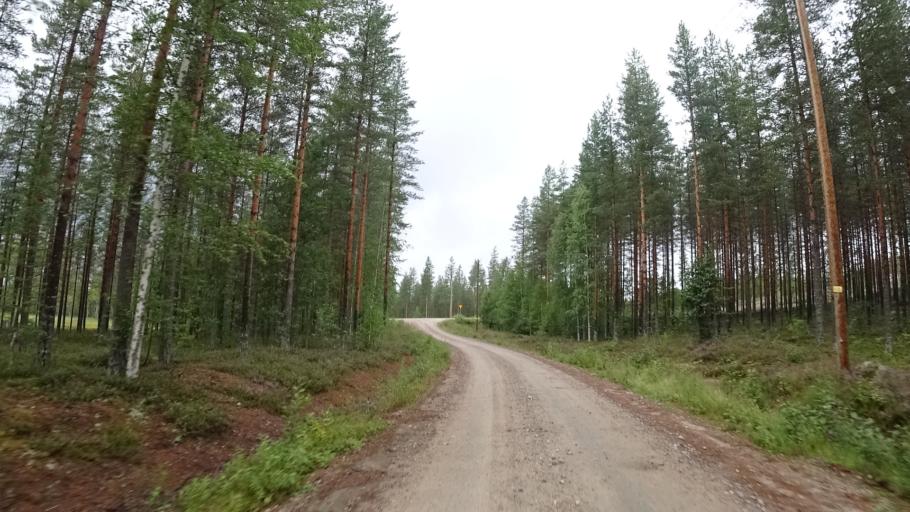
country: FI
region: North Karelia
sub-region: Pielisen Karjala
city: Lieksa
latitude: 63.5398
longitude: 30.0431
